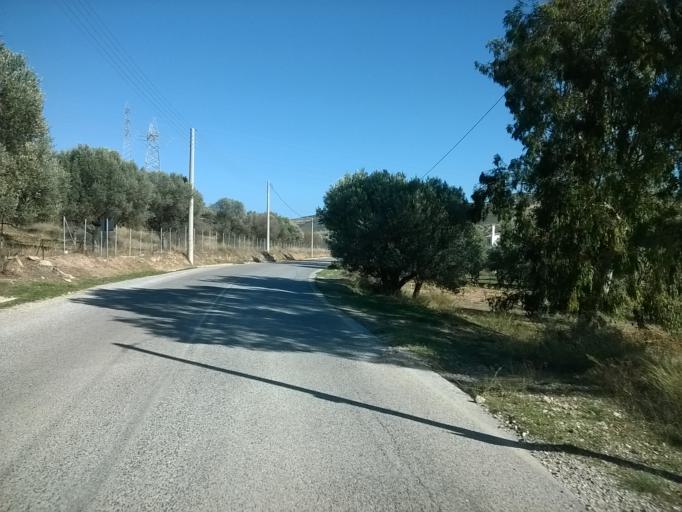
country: GR
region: Attica
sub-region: Nomarchia Anatolikis Attikis
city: Keratea
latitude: 37.7790
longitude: 24.0033
